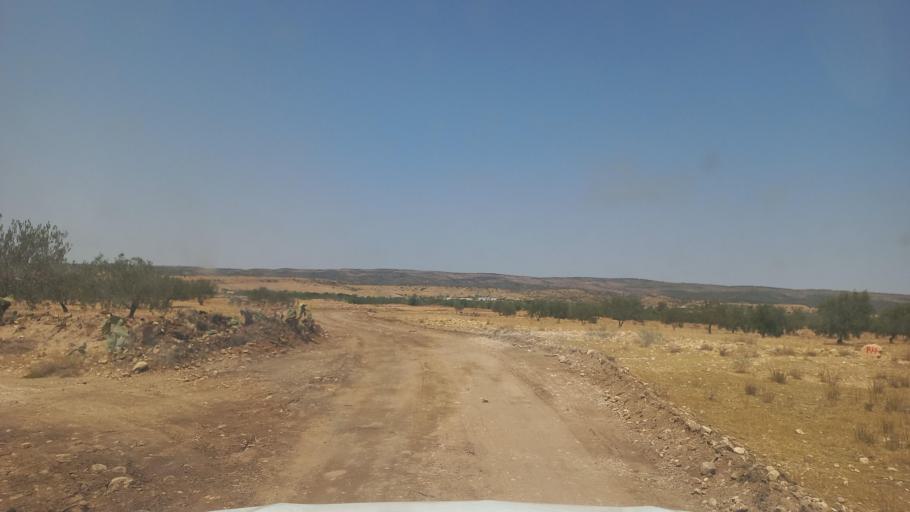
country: TN
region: Al Qasrayn
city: Kasserine
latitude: 35.2921
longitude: 8.9526
